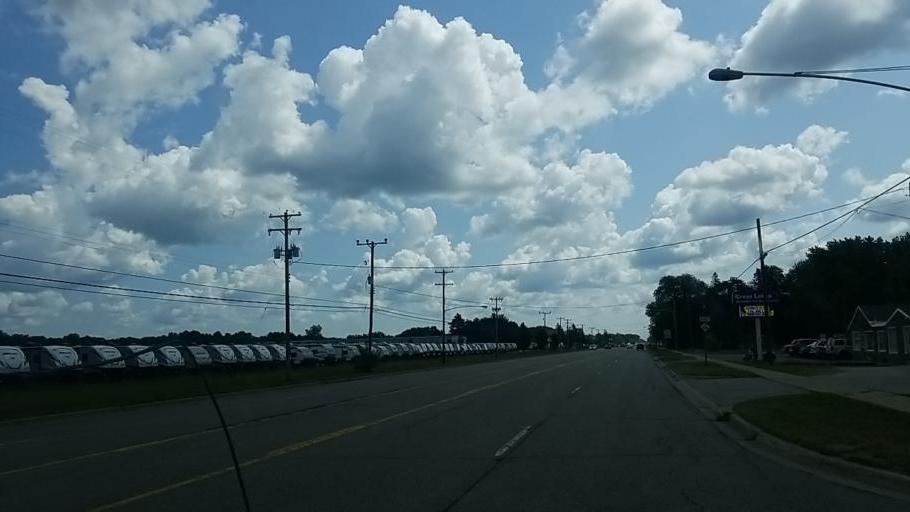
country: US
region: Michigan
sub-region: Muskegon County
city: Wolf Lake
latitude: 43.2346
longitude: -86.1366
